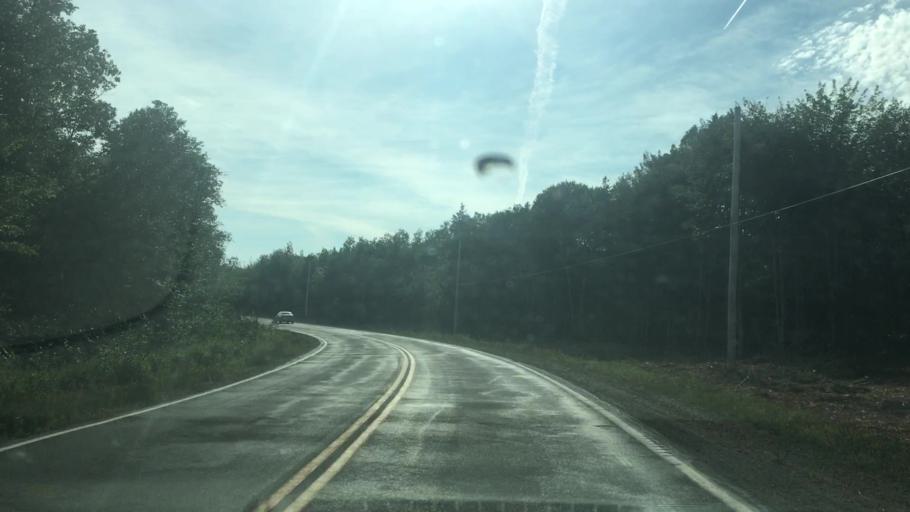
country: CA
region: Nova Scotia
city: Sydney Mines
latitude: 46.8816
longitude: -60.5143
